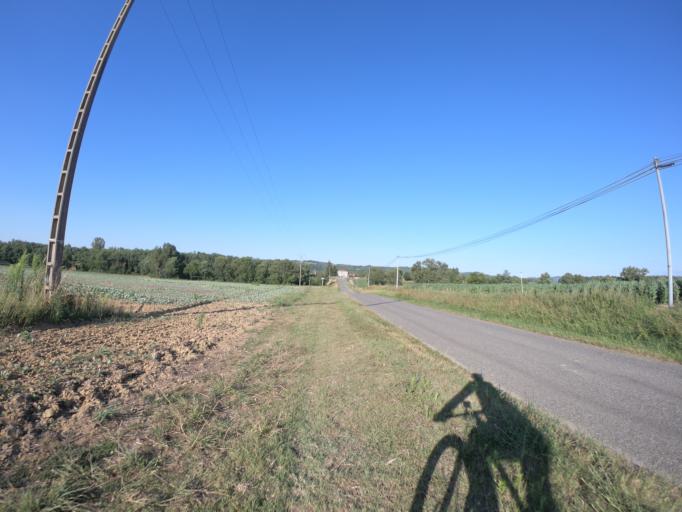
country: FR
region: Midi-Pyrenees
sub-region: Departement de l'Ariege
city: La Tour-du-Crieu
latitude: 43.0960
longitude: 1.7301
